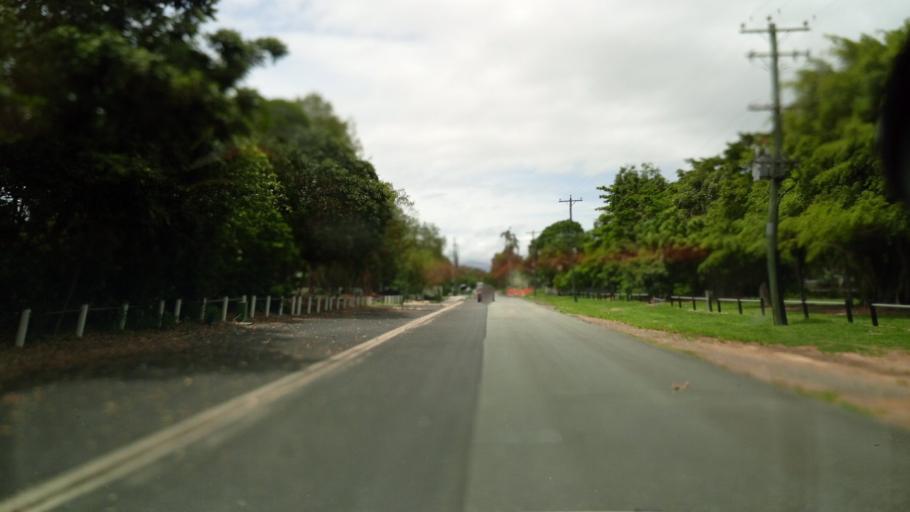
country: AU
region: Queensland
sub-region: Cairns
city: Redlynch
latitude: -16.8539
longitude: 145.7512
